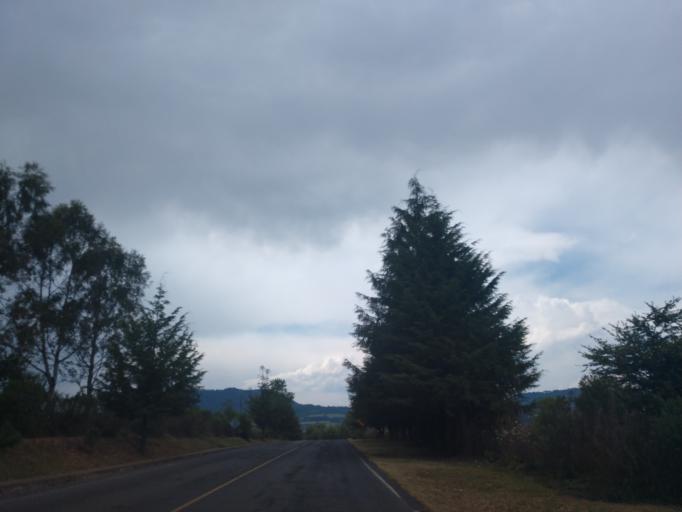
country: MX
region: Jalisco
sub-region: Mazamitla
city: Mazamitla
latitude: 19.9222
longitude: -103.0391
